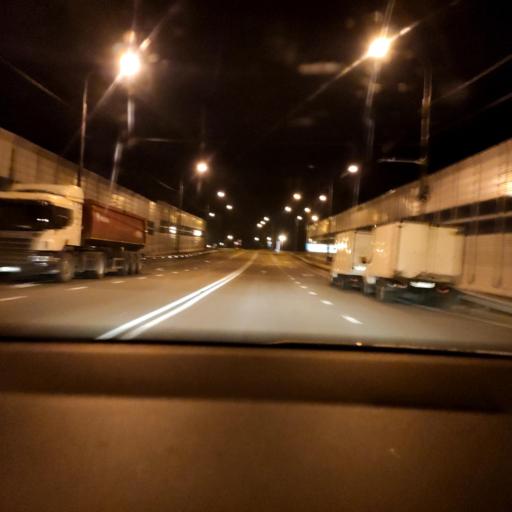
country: RU
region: Moskovskaya
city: Bolshevo
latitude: 55.9505
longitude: 37.8298
